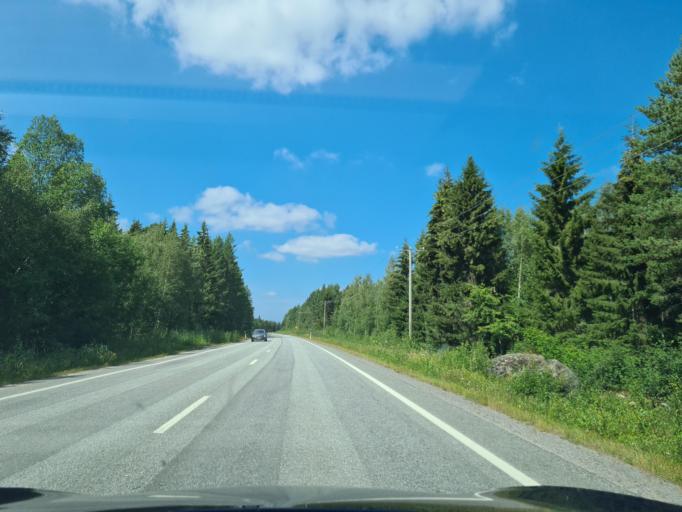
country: FI
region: Ostrobothnia
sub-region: Vaasa
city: Vaasa
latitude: 63.1792
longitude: 21.5745
